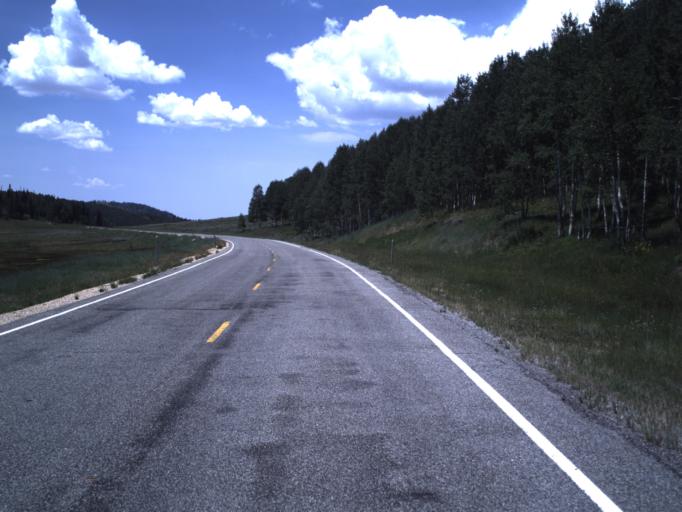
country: US
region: Utah
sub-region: Sanpete County
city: Fairview
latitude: 39.6513
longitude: -111.2784
